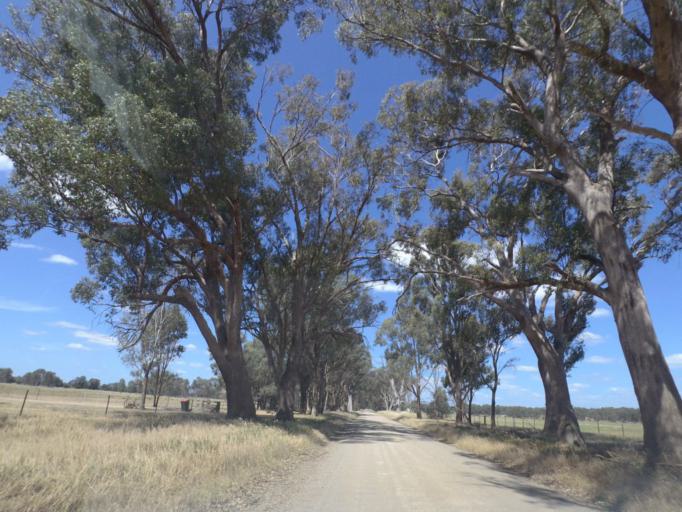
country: AU
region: Victoria
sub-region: Wangaratta
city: Wangaratta
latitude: -36.3998
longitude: 146.2914
